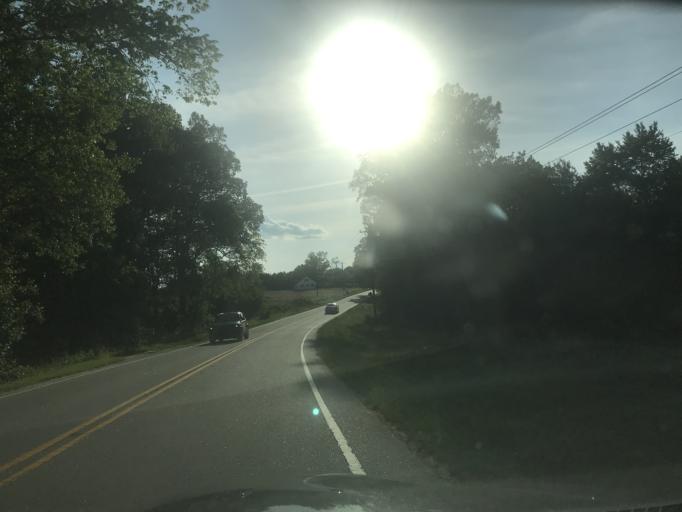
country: US
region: North Carolina
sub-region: Wake County
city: Knightdale
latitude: 35.7517
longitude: -78.4913
